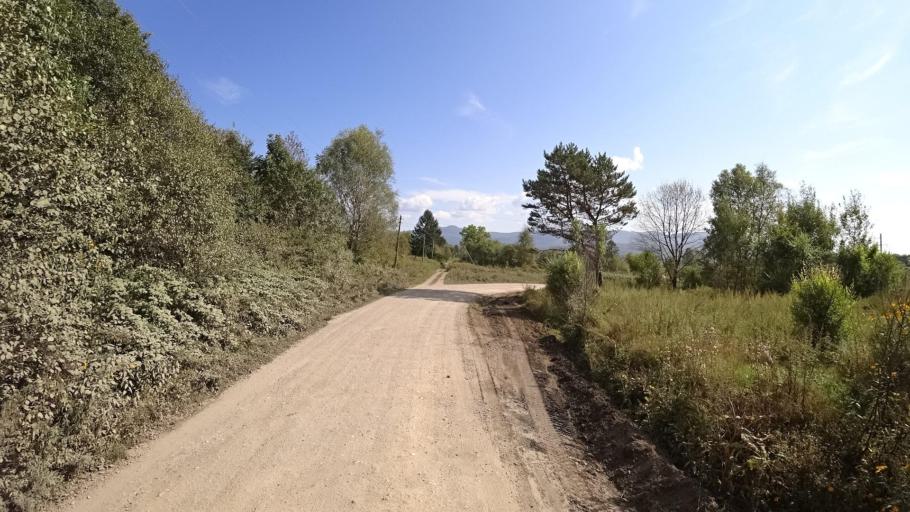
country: RU
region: Jewish Autonomous Oblast
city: Birakan
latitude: 49.0092
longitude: 131.7377
